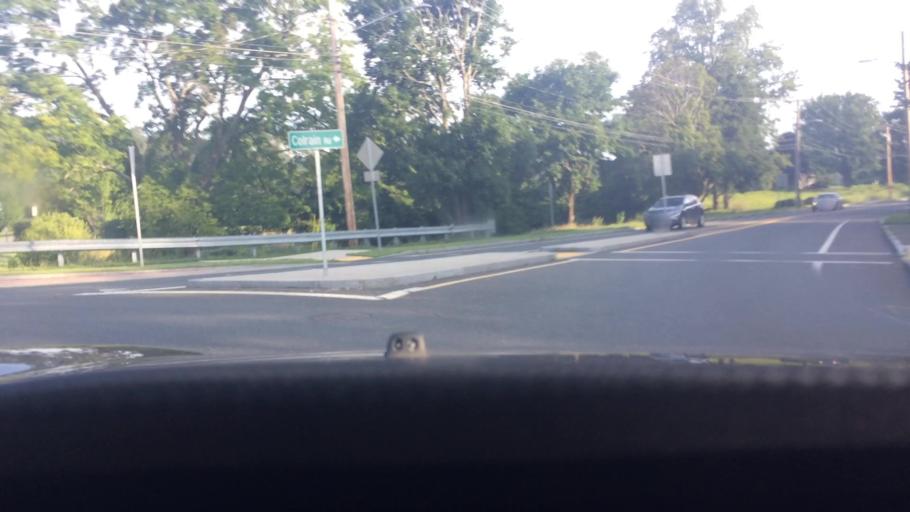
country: US
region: Massachusetts
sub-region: Franklin County
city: Greenfield
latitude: 42.5941
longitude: -72.6200
